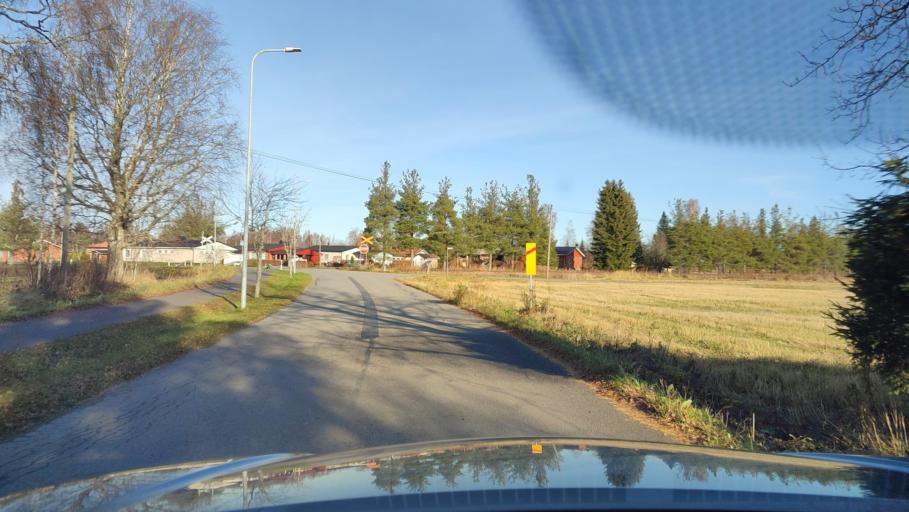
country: FI
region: Southern Ostrobothnia
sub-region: Suupohja
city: Teuva
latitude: 62.4763
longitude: 21.7513
